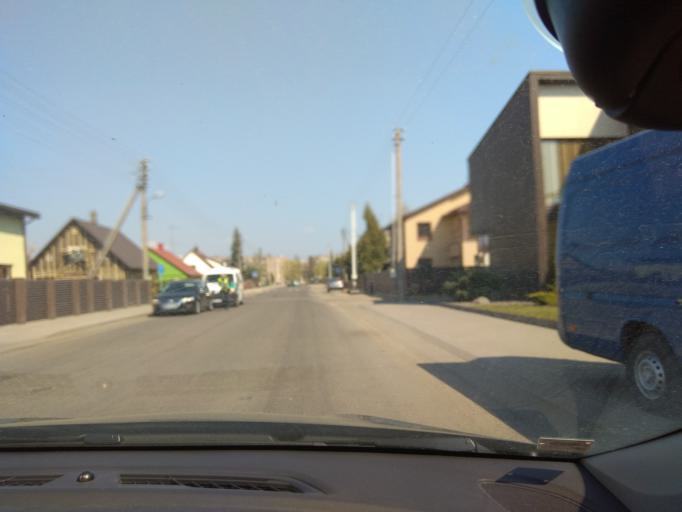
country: LT
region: Marijampoles apskritis
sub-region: Marijampole Municipality
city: Marijampole
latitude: 54.5651
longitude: 23.3502
